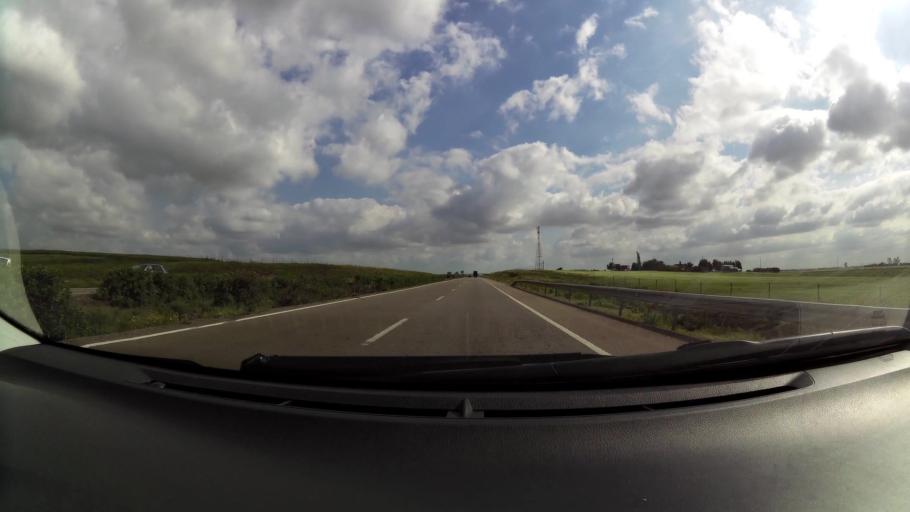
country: MA
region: Chaouia-Ouardigha
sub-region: Settat Province
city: Berrechid
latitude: 33.2136
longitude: -7.5750
